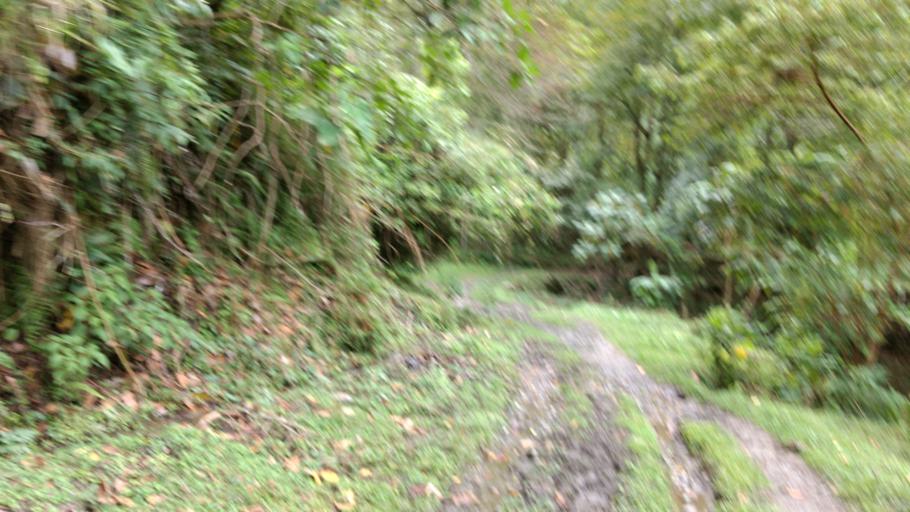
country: CO
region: Tolima
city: Cajamarca
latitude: 4.5483
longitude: -75.3339
